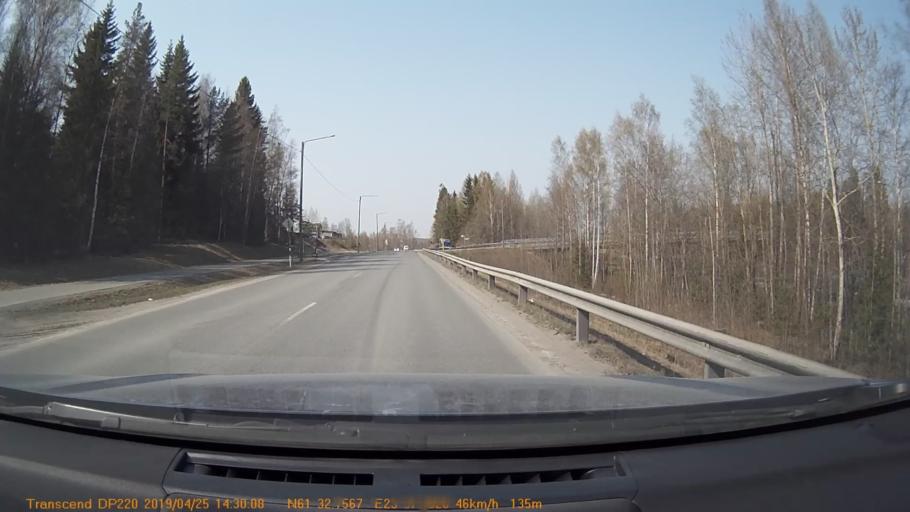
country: FI
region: Pirkanmaa
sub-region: Tampere
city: Yloejaervi
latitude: 61.5361
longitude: 23.6229
